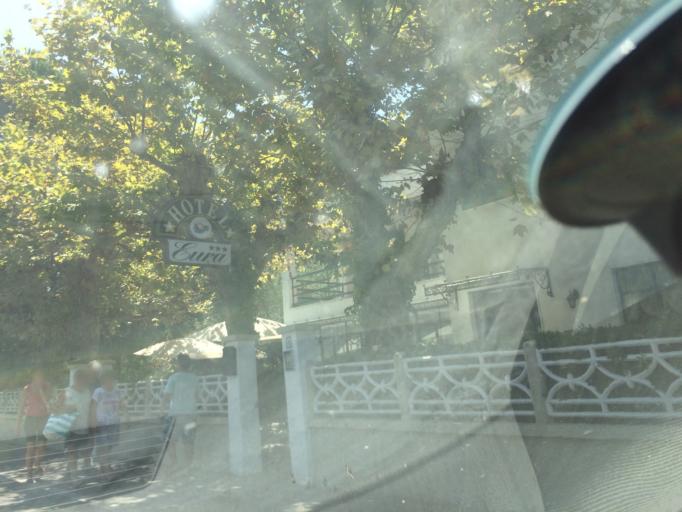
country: IT
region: Tuscany
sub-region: Provincia di Massa-Carrara
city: Massa
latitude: 44.0115
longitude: 10.0975
